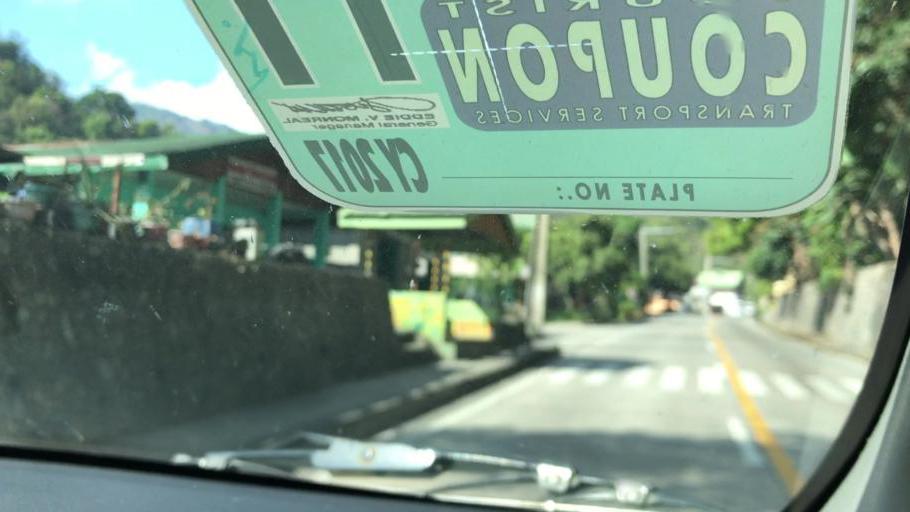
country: PH
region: Cordillera
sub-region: Province of Benguet
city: Tuba
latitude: 16.3142
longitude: 120.6177
